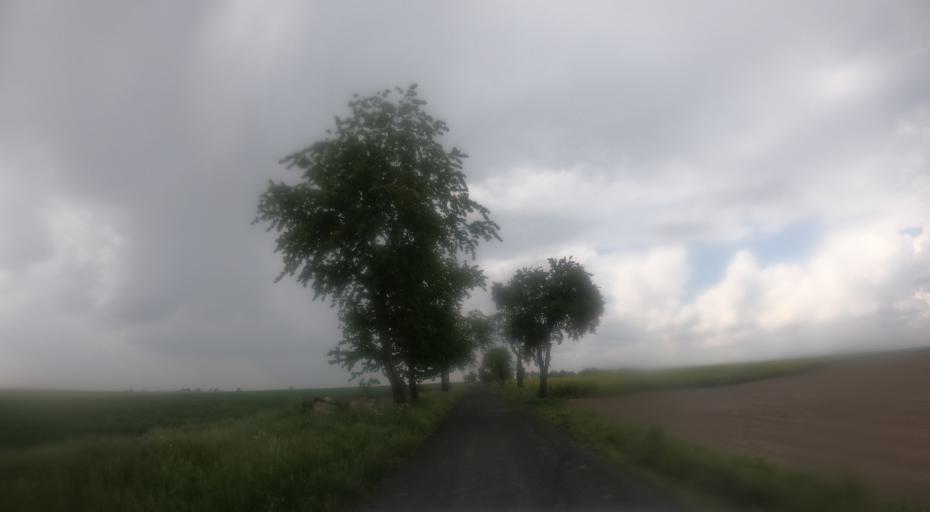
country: PL
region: West Pomeranian Voivodeship
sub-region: Powiat pyrzycki
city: Bielice
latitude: 53.2585
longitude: 14.7055
